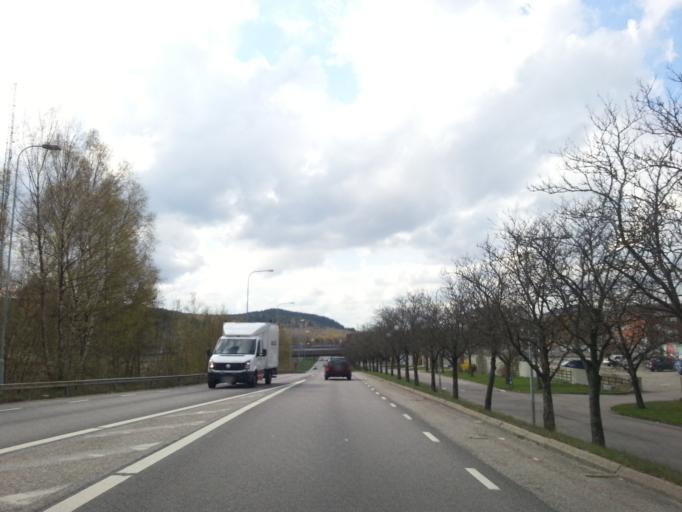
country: SE
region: Vaestra Goetaland
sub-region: Goteborg
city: Hammarkullen
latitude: 57.7723
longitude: 12.0232
